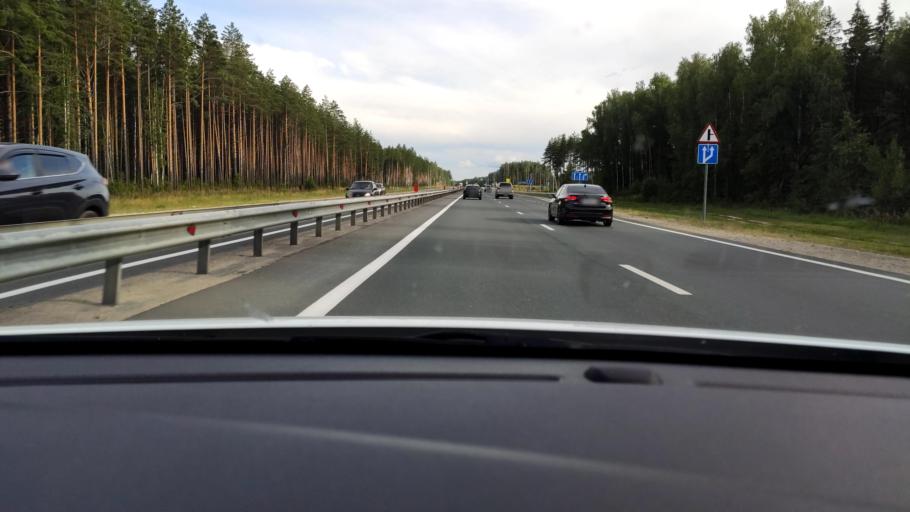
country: RU
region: Mariy-El
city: Surok
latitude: 56.5211
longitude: 48.0113
